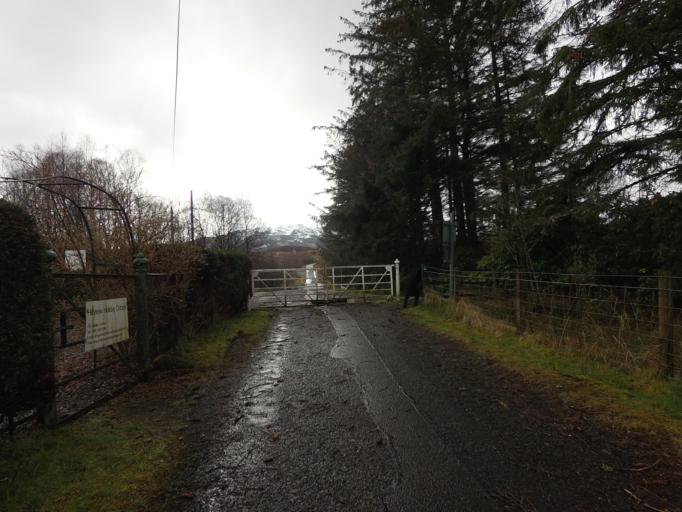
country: GB
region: Scotland
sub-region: West Dunbartonshire
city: Balloch
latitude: 56.2569
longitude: -4.5829
